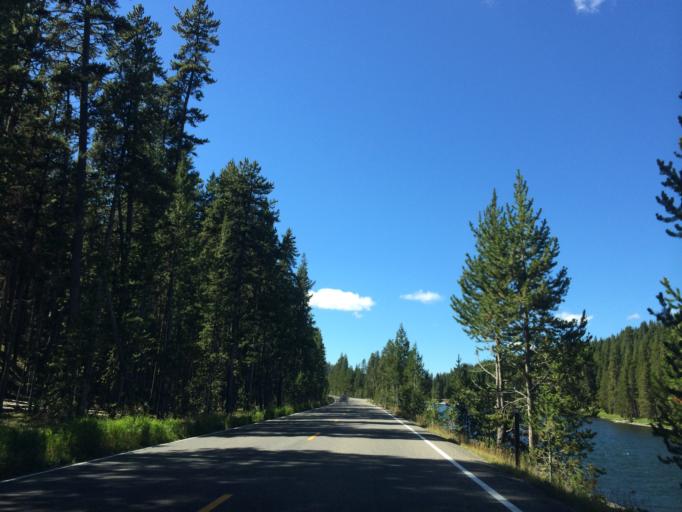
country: US
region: Montana
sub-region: Gallatin County
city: West Yellowstone
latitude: 44.6082
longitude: -110.3898
